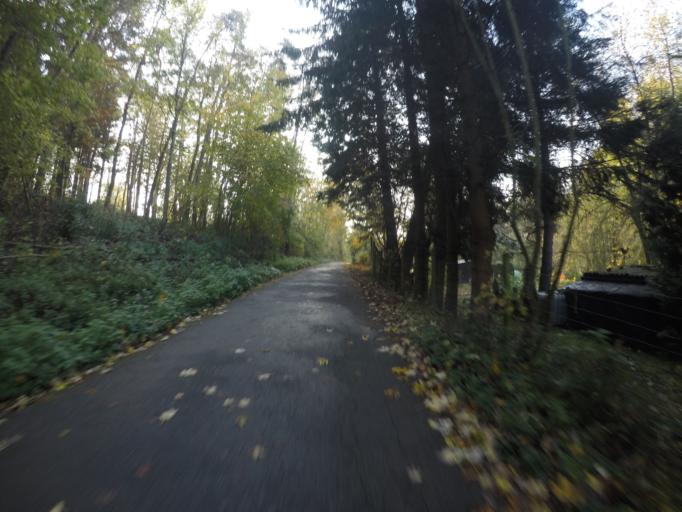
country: DE
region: Baden-Wuerttemberg
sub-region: Regierungsbezirk Stuttgart
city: Leinfelden-Echterdingen
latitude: 48.7113
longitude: 9.1832
